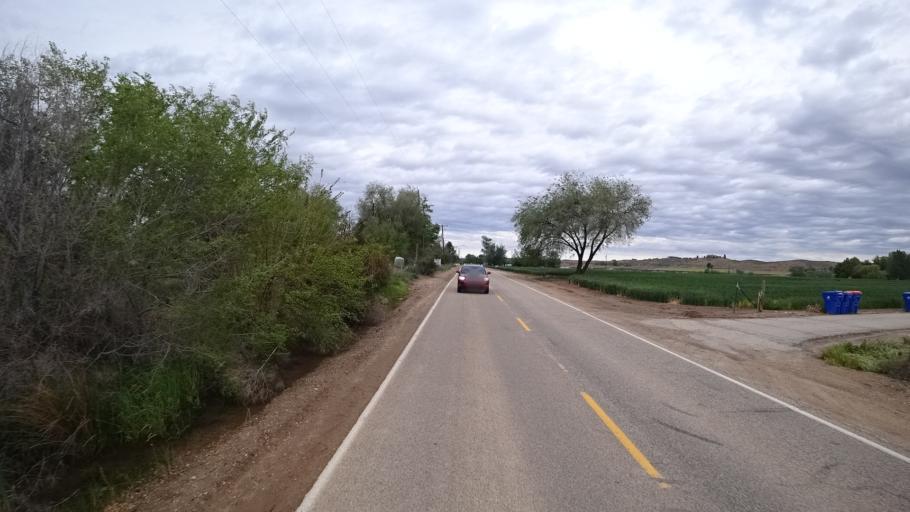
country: US
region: Idaho
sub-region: Ada County
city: Star
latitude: 43.7212
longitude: -116.4757
